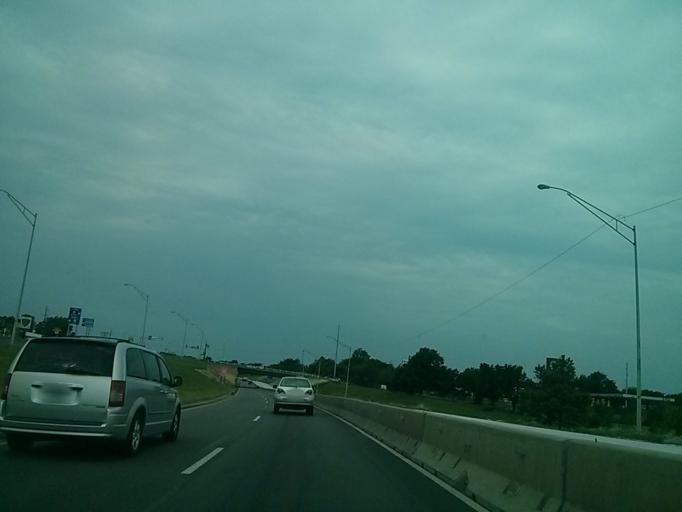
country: US
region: Oklahoma
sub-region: Tulsa County
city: Tulsa
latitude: 36.1634
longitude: -95.9016
